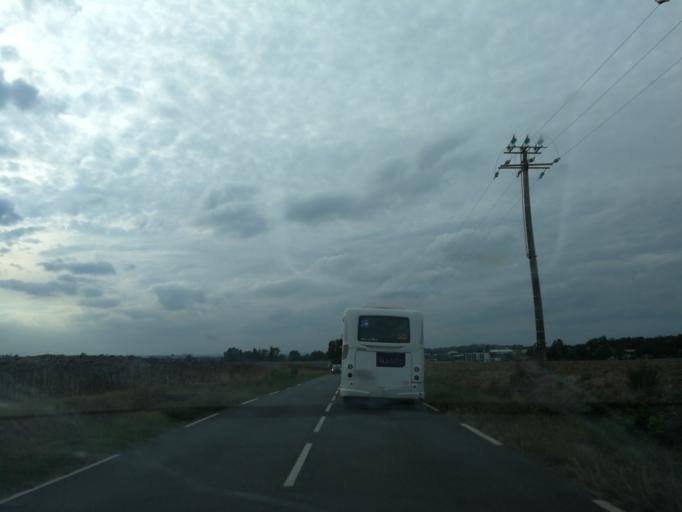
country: FR
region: Midi-Pyrenees
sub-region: Departement de la Haute-Garonne
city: Flourens
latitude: 43.5963
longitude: 1.5530
